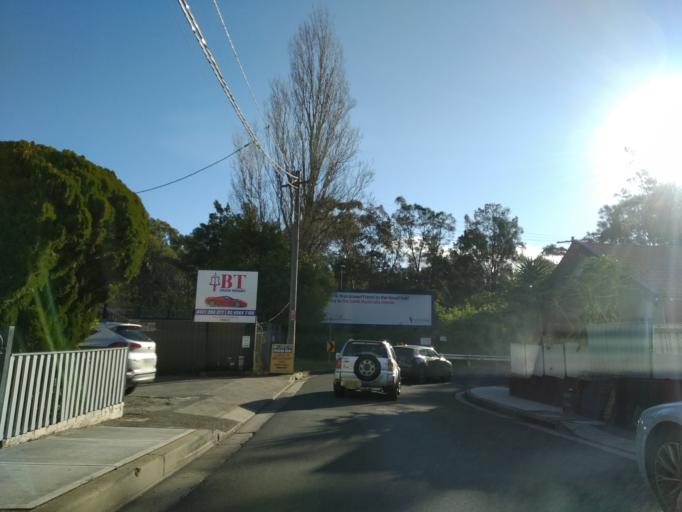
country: AU
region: New South Wales
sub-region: Marrickville
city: Lewisham
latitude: -33.8917
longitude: 151.1455
